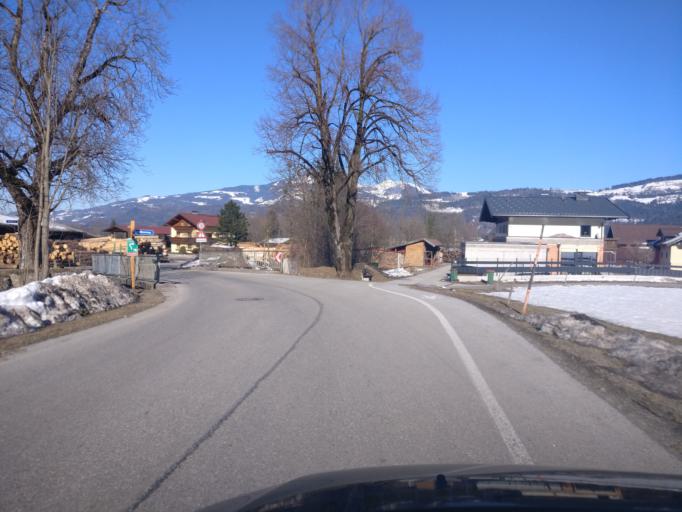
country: AT
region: Salzburg
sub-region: Politischer Bezirk Hallein
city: Kuchl
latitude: 47.6129
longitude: 13.1427
